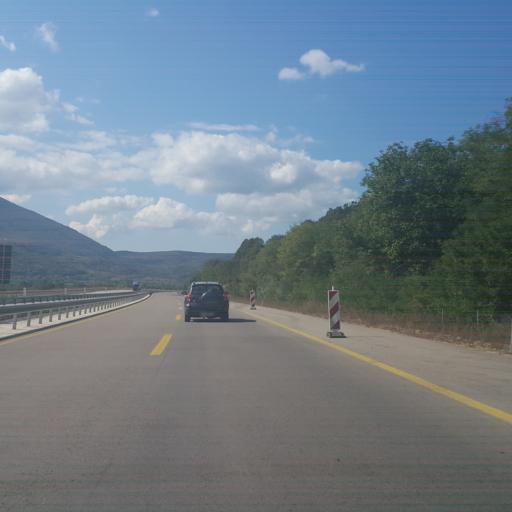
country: RS
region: Central Serbia
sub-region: Pirotski Okrug
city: Bela Palanka
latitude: 43.2368
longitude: 22.3020
